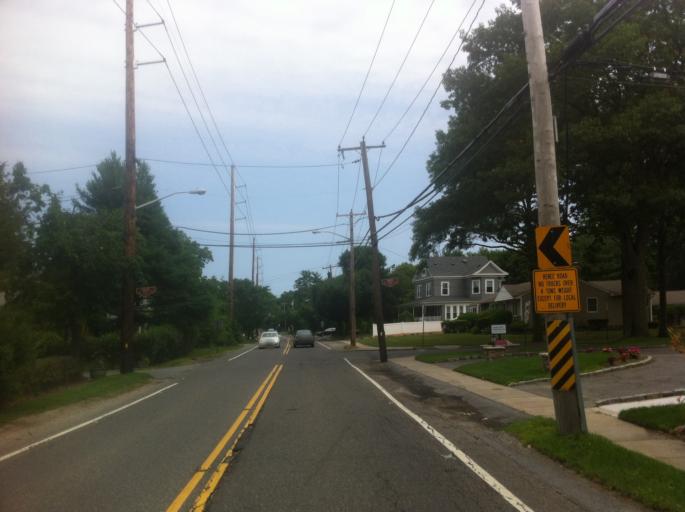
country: US
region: New York
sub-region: Nassau County
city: Syosset
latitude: 40.8321
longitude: -73.5000
